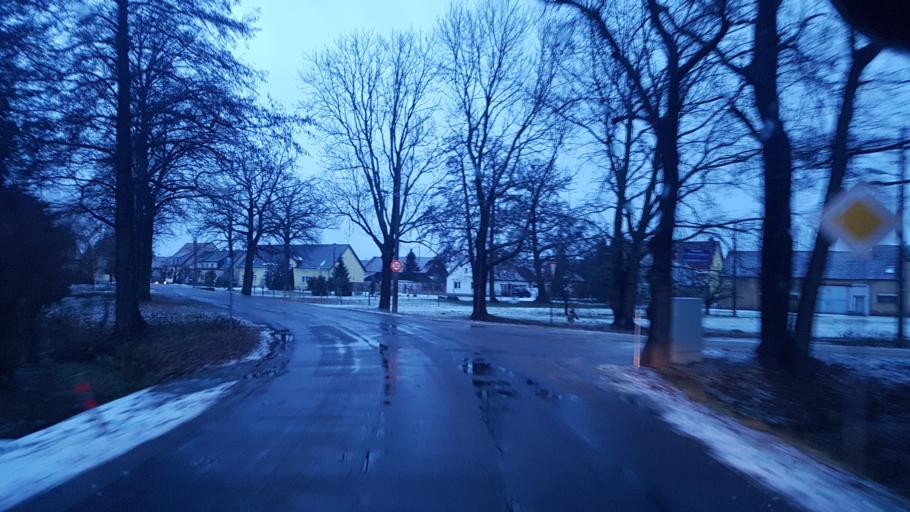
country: DE
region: Brandenburg
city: Drehnow
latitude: 51.8237
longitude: 14.3402
